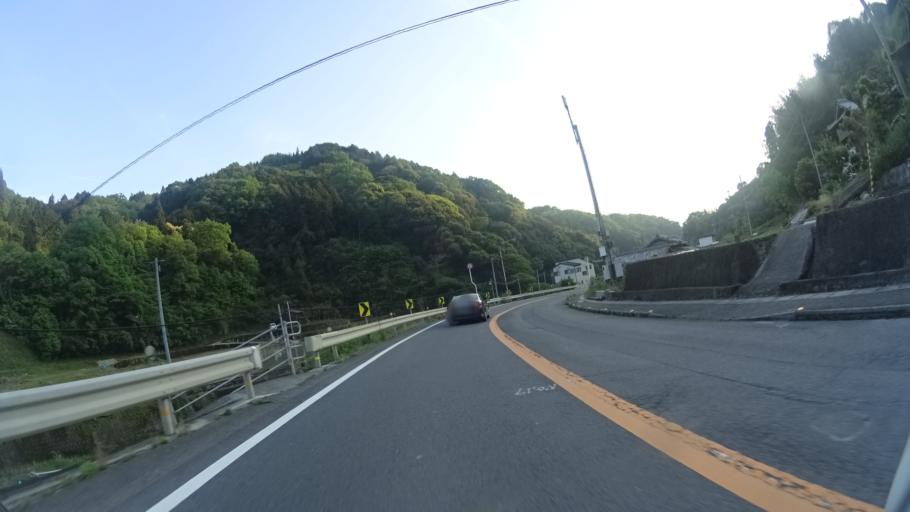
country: JP
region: Ehime
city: Kawanoecho
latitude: 33.9952
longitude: 133.6520
